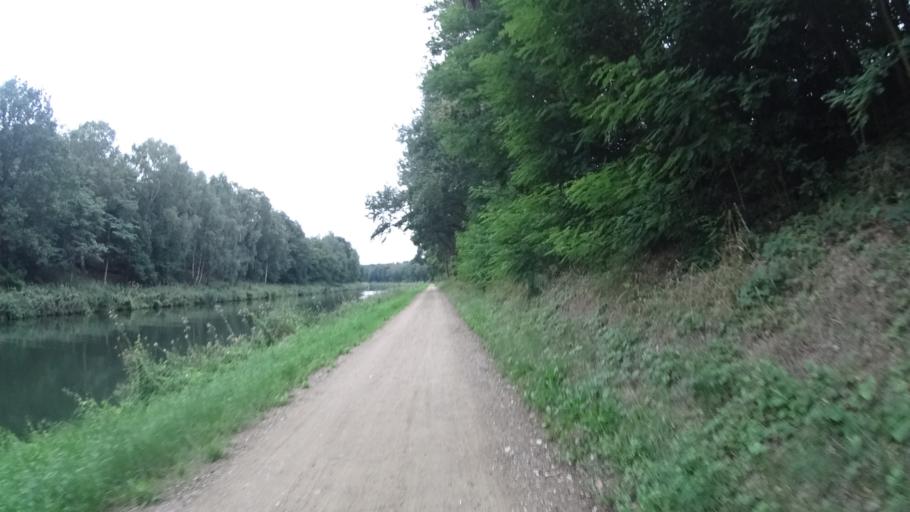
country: DE
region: Schleswig-Holstein
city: Grambek
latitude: 53.5908
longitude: 10.6658
